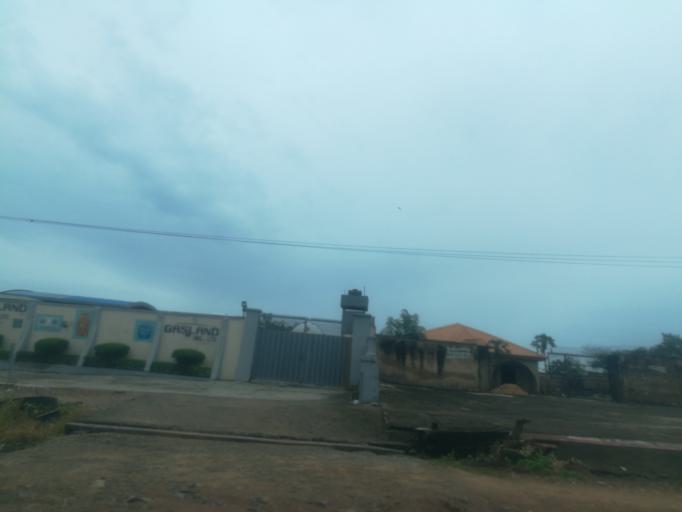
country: NG
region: Oyo
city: Ibadan
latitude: 7.3348
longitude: 3.8888
